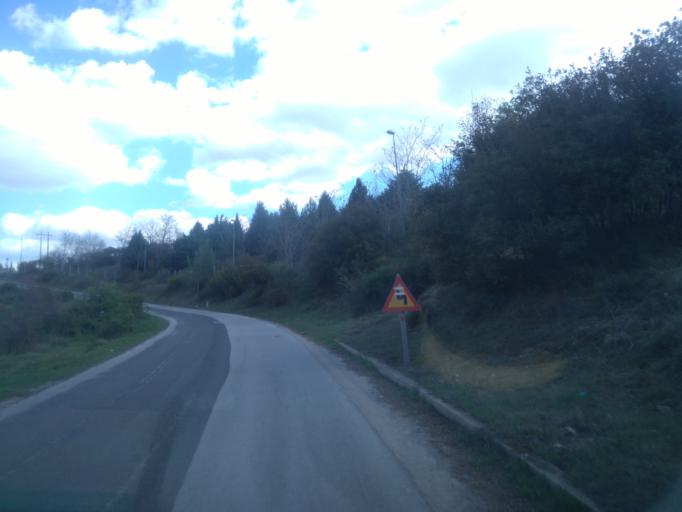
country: GR
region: Central Macedonia
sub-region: Nomos Thessalonikis
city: Asvestochori
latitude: 40.6354
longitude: 23.0207
